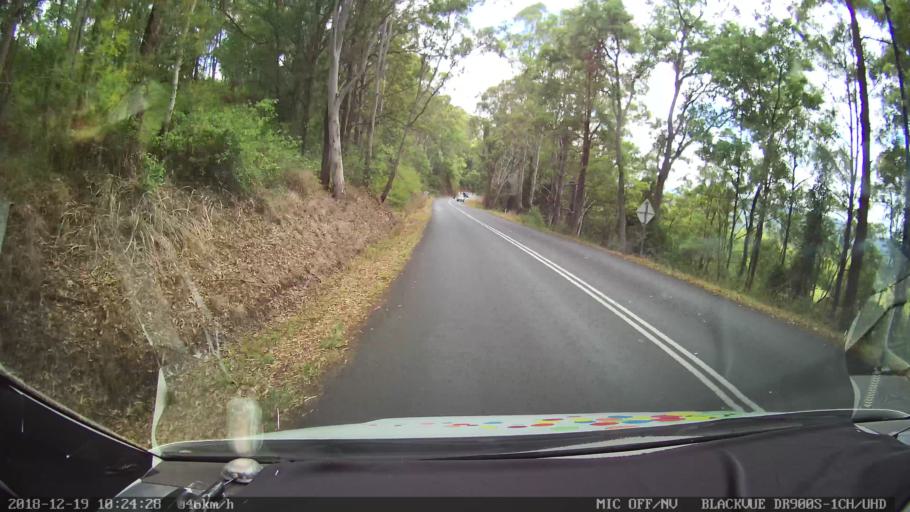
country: AU
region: New South Wales
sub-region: Lismore Municipality
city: Larnook
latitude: -28.5949
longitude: 153.0784
